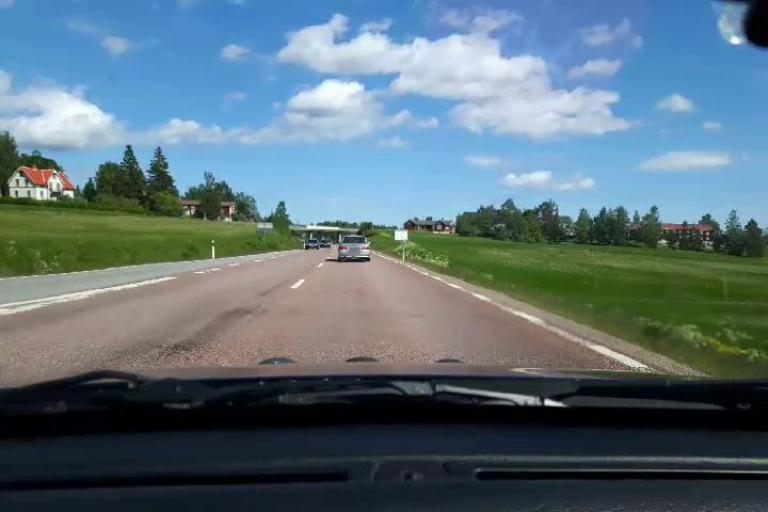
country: SE
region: Gaevleborg
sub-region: Hudiksvalls Kommun
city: Sorforsa
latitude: 61.7396
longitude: 16.8799
